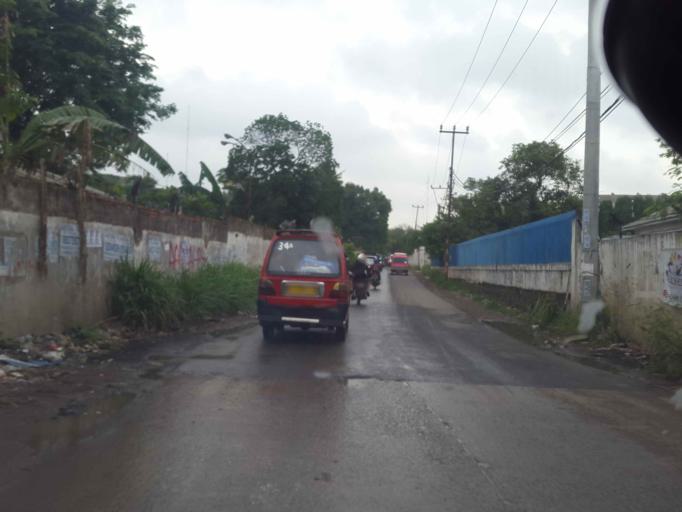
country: ID
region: West Java
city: Bekasi
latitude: -6.2549
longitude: 107.0415
